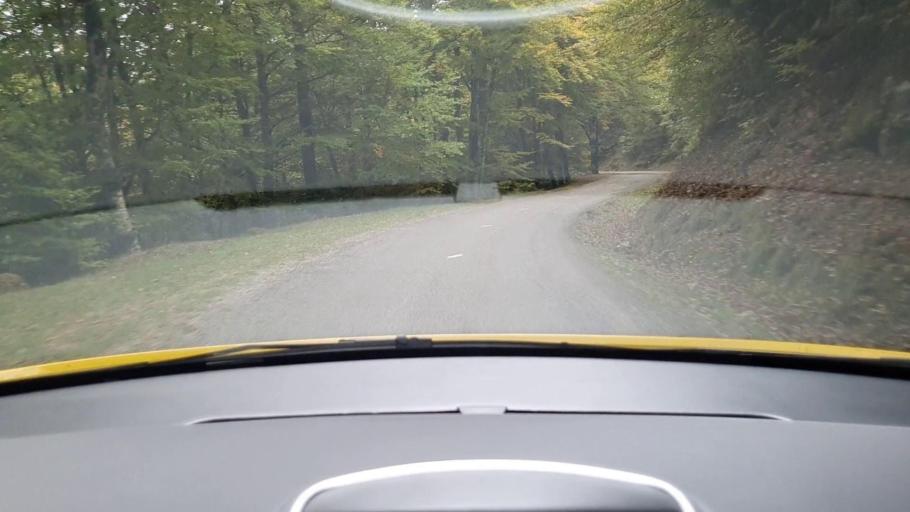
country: FR
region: Languedoc-Roussillon
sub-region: Departement de la Lozere
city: Meyrueis
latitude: 44.0897
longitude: 3.4479
